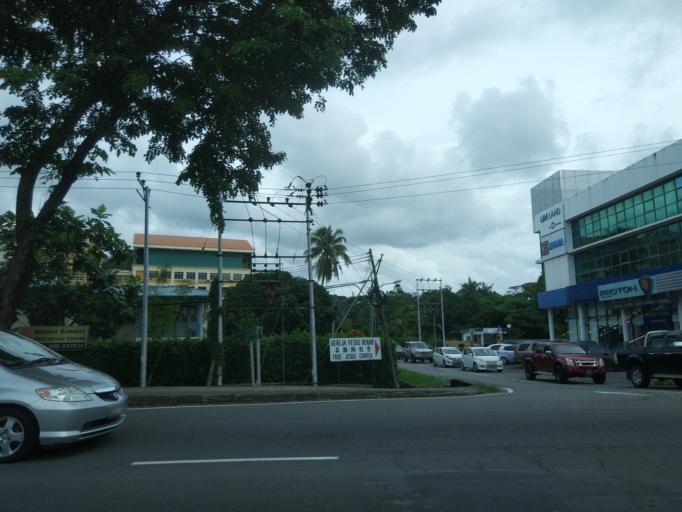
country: MY
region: Sabah
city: Kota Kinabalu
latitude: 5.9770
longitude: 116.0971
